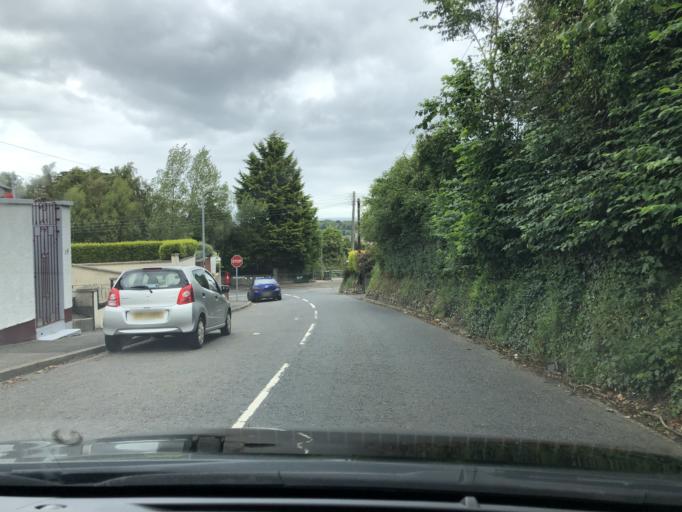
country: GB
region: Northern Ireland
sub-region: Larne District
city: Larne
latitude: 54.8473
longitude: -5.8297
